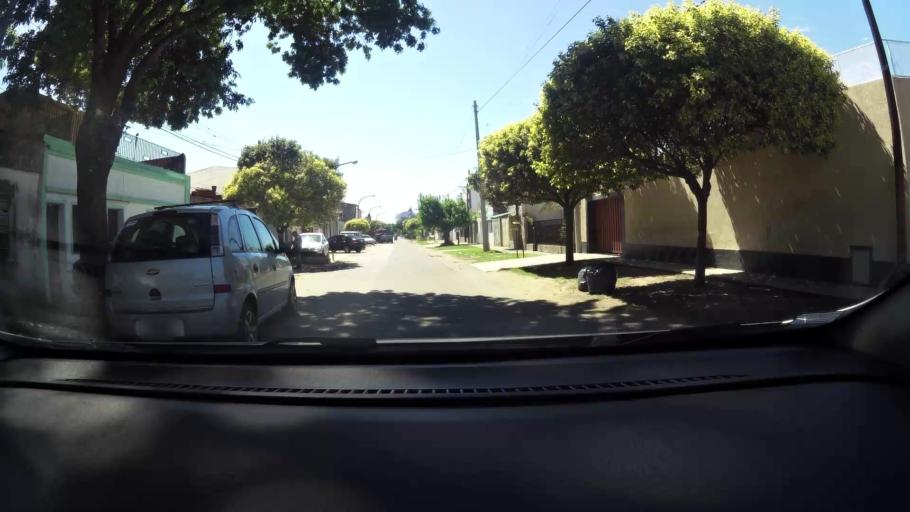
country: AR
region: Santa Fe
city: Perez
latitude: -32.9667
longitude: -60.7163
